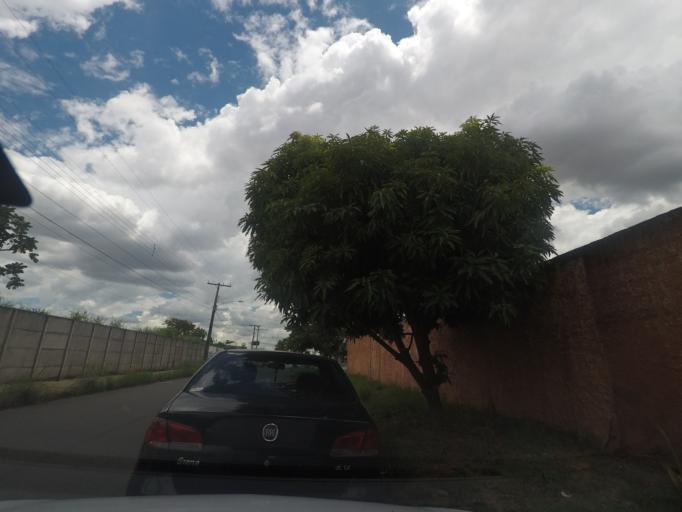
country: BR
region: Goias
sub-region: Goiania
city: Goiania
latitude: -16.7491
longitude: -49.3217
